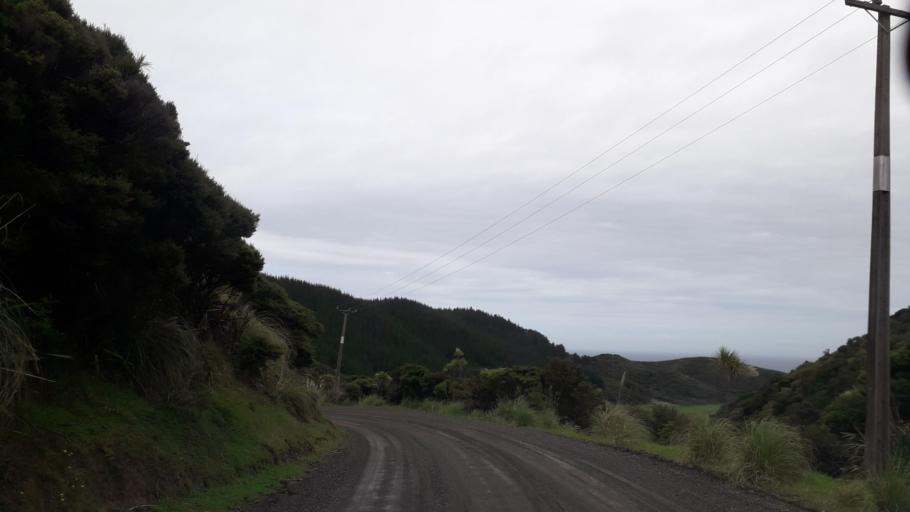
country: NZ
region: Northland
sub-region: Far North District
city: Ahipara
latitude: -35.4388
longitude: 173.3043
